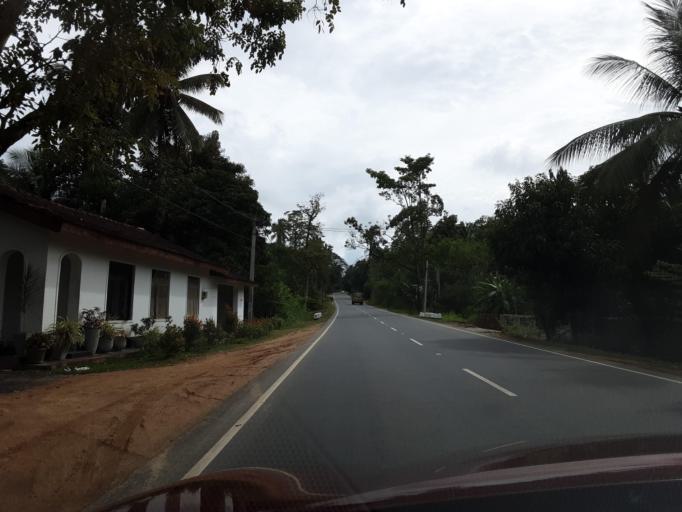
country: LK
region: Eastern Province
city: Eravur Town
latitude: 7.5197
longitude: 81.3440
